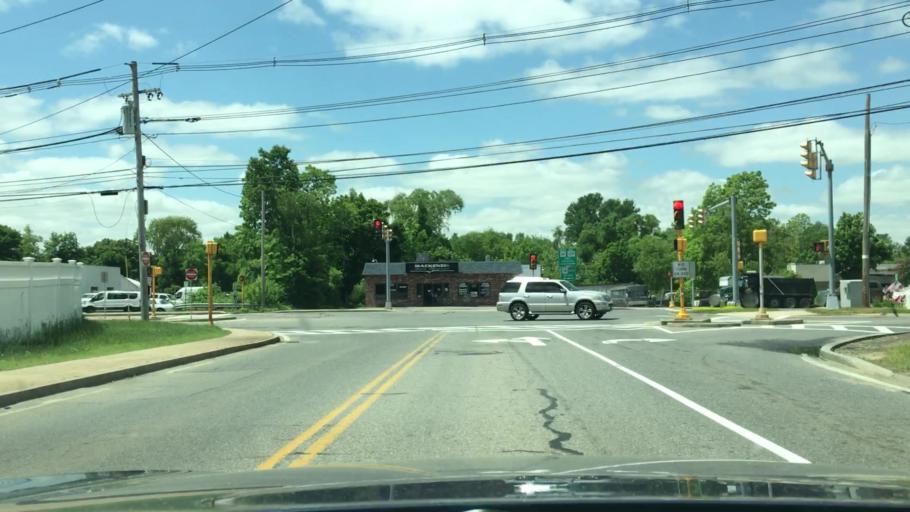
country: US
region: Massachusetts
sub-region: Middlesex County
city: Billerica
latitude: 42.5711
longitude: -71.2761
